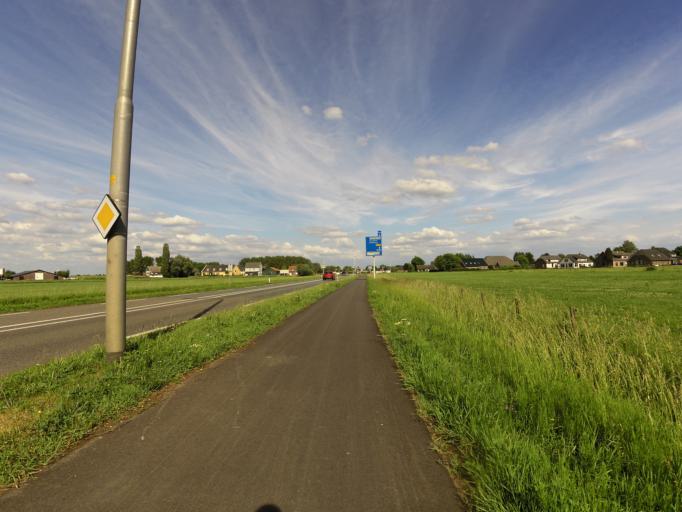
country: NL
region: Gelderland
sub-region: Gemeente Rheden
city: Rheden
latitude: 51.9852
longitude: 6.0221
